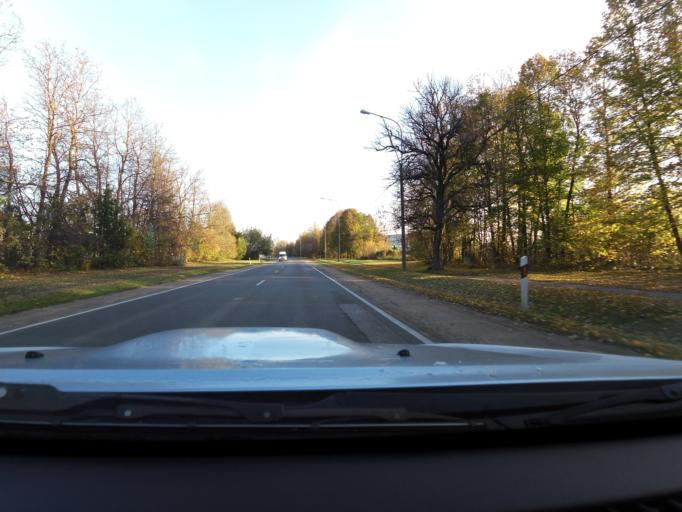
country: LT
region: Vilnius County
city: Vilkpede
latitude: 54.6401
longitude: 25.2602
